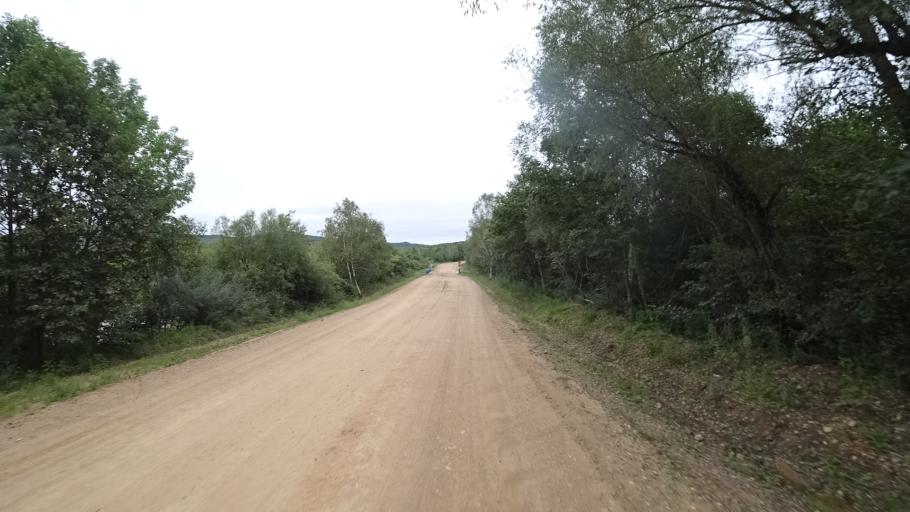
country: RU
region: Primorskiy
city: Rettikhovka
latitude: 44.1726
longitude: 132.7963
